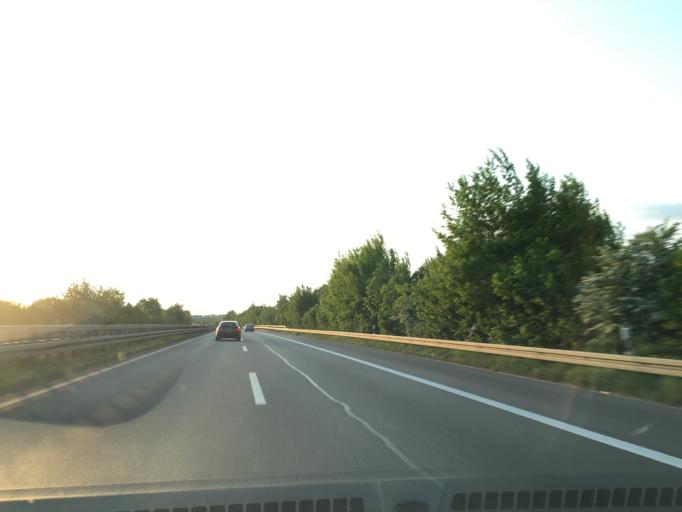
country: DE
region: Lower Saxony
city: Melle
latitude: 52.2039
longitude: 8.3051
